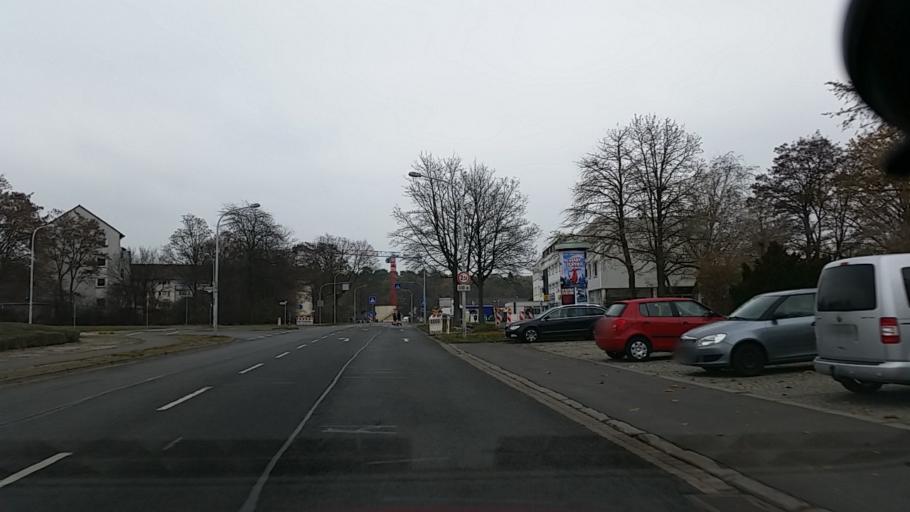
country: DE
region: Lower Saxony
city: Wolfsburg
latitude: 52.4523
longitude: 10.8046
